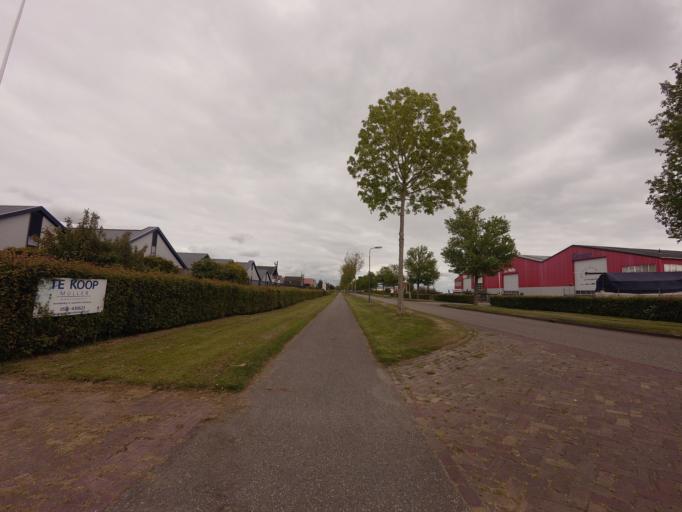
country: NL
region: Friesland
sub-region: Sudwest Fryslan
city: Woudsend
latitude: 52.9429
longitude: 5.6375
